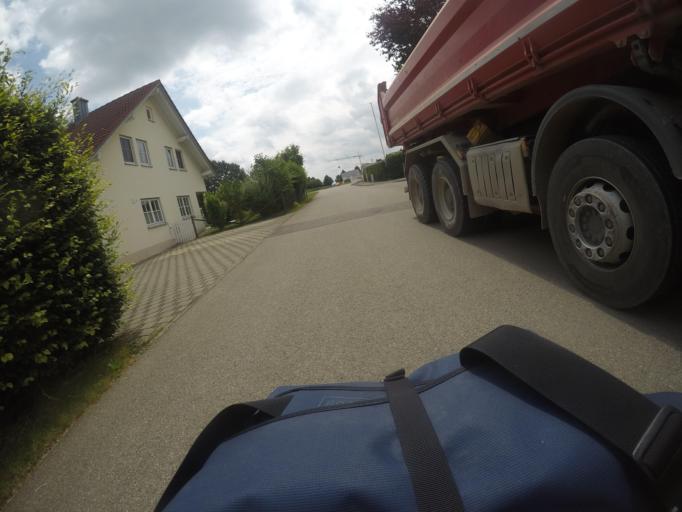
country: DE
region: Bavaria
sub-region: Swabia
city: Fellheim
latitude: 48.0731
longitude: 10.1563
